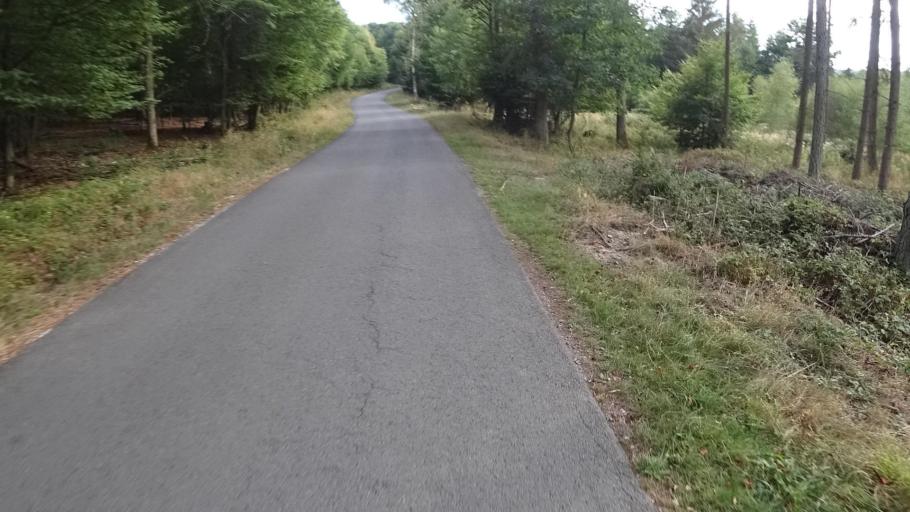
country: DE
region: Rheinland-Pfalz
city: Dichtelbach
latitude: 49.9973
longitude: 7.7049
